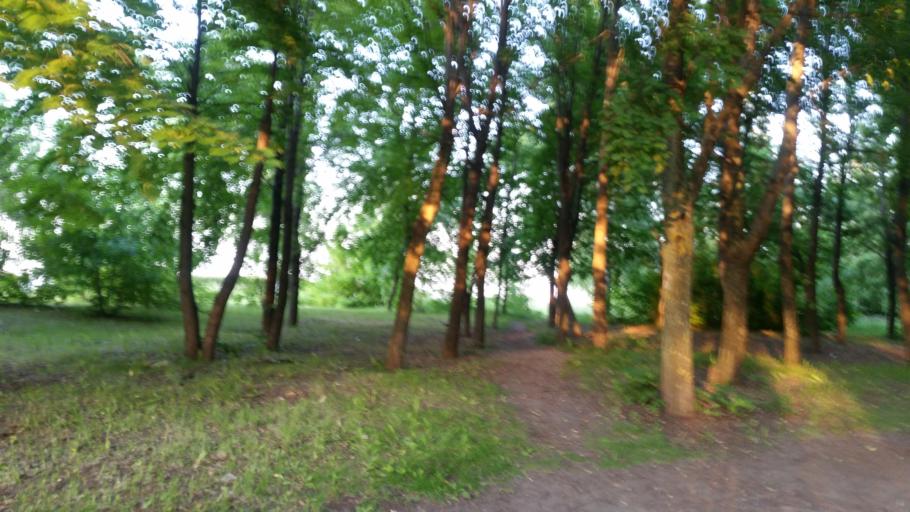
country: RU
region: Ulyanovsk
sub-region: Ulyanovskiy Rayon
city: Ulyanovsk
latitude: 54.3497
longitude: 48.3932
